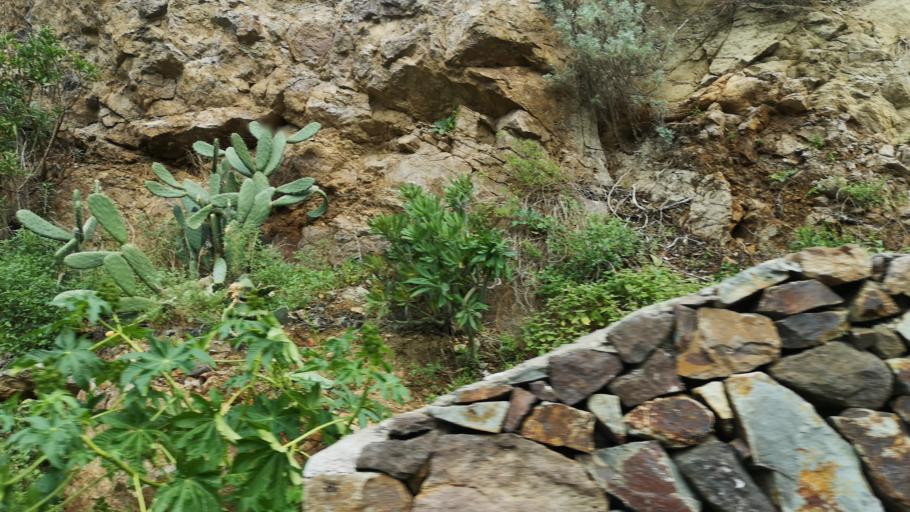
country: ES
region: Canary Islands
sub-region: Provincia de Santa Cruz de Tenerife
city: Vallehermosa
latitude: 28.1719
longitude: -17.2768
